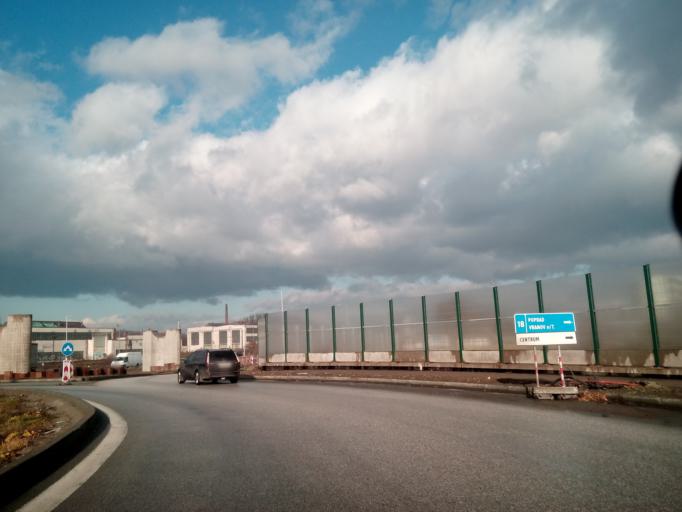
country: SK
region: Presovsky
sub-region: Okres Presov
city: Presov
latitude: 48.9705
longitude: 21.2540
